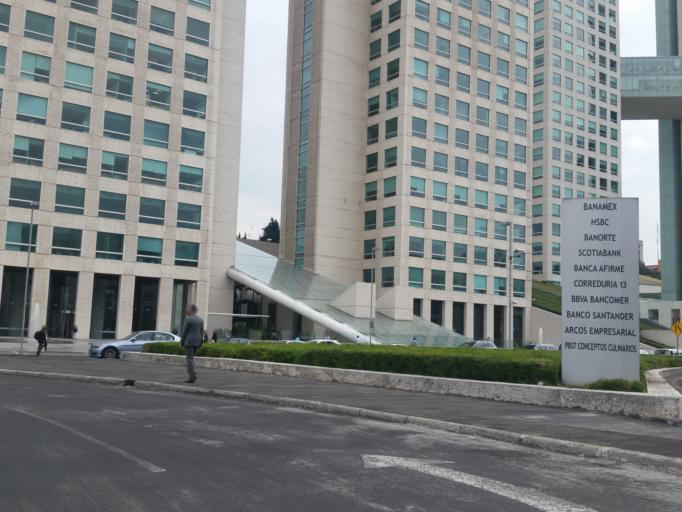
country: MX
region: Mexico City
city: Col. Bosques de las Lomas
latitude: 19.3887
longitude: -99.2512
